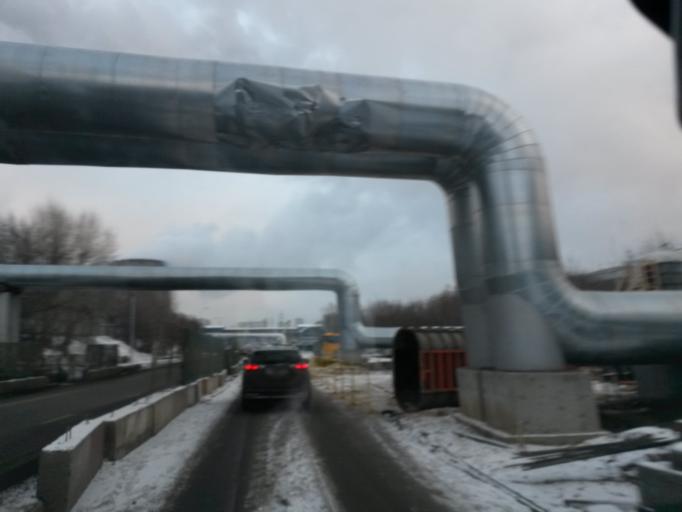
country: RU
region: Moscow
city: Ochakovo-Matveyevskoye
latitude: 55.6934
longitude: 37.4477
